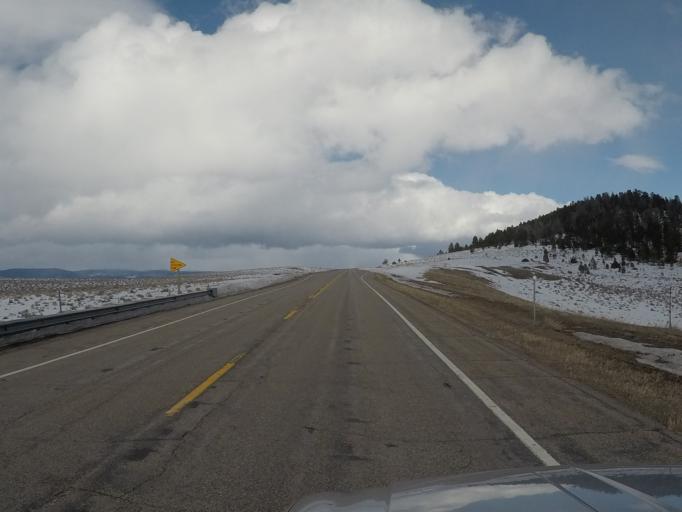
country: US
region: Montana
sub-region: Meagher County
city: White Sulphur Springs
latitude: 46.6126
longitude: -110.7568
